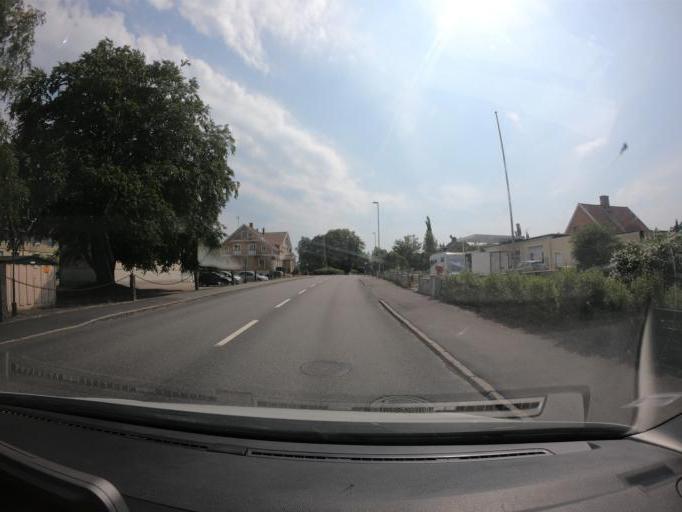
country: SE
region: Skane
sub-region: Hassleholms Kommun
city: Bjarnum
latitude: 56.3468
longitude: 13.6621
